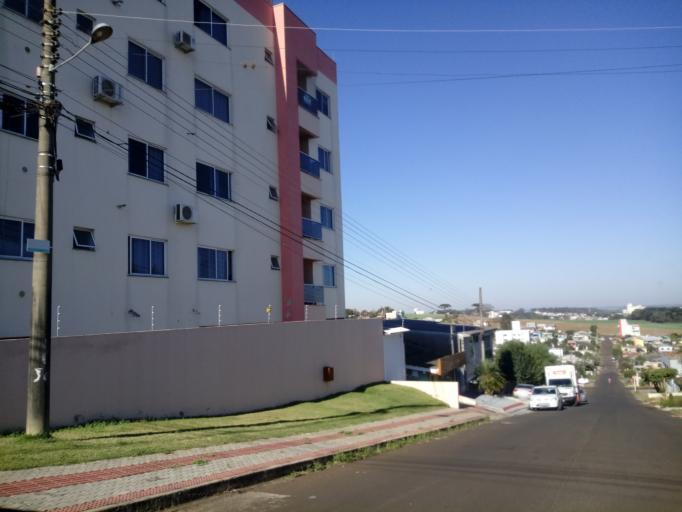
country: BR
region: Santa Catarina
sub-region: Chapeco
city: Chapeco
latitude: -27.0782
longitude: -52.6331
